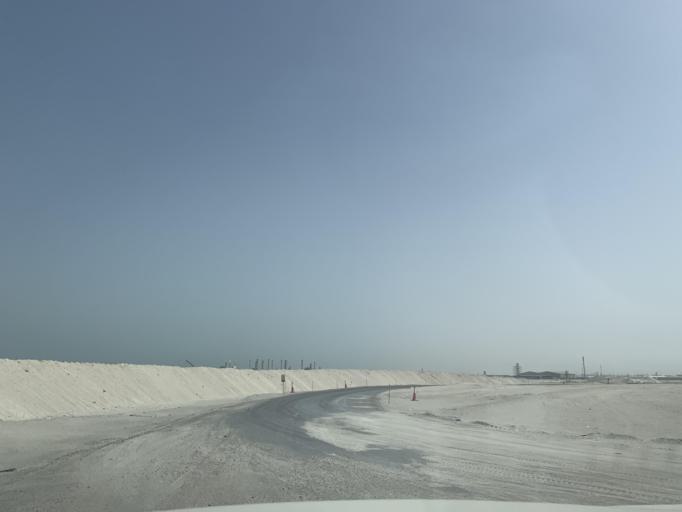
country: BH
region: Northern
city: Sitrah
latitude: 26.1599
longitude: 50.6427
